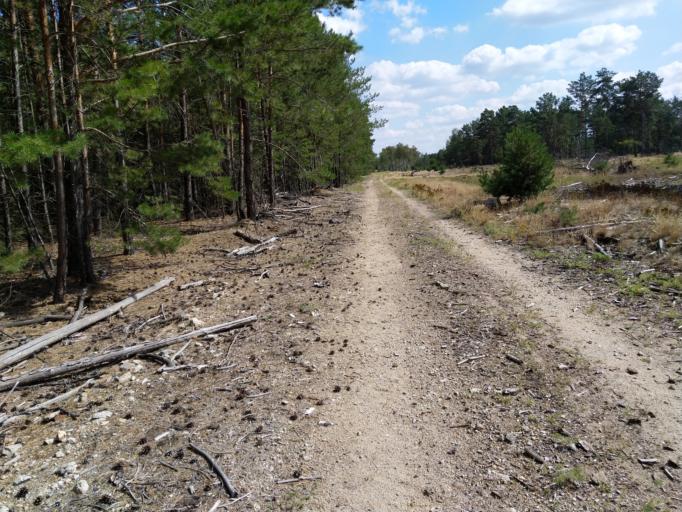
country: DE
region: Brandenburg
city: Luckenwalde
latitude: 52.0390
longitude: 13.1830
